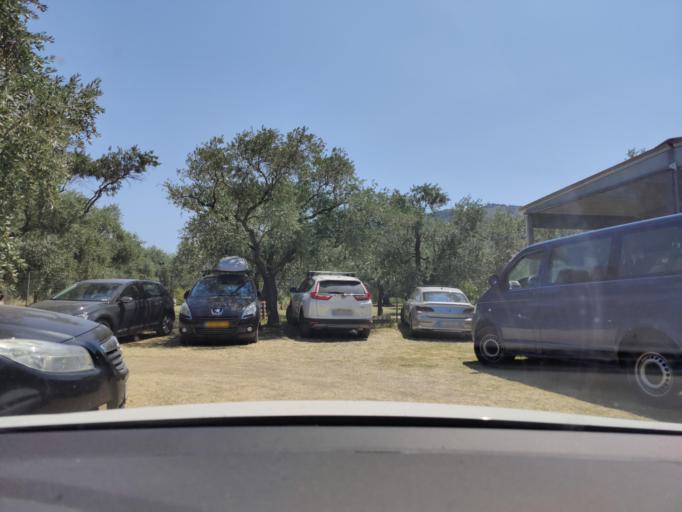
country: GR
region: East Macedonia and Thrace
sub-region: Nomos Kavalas
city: Prinos
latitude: 40.7701
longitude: 24.5935
